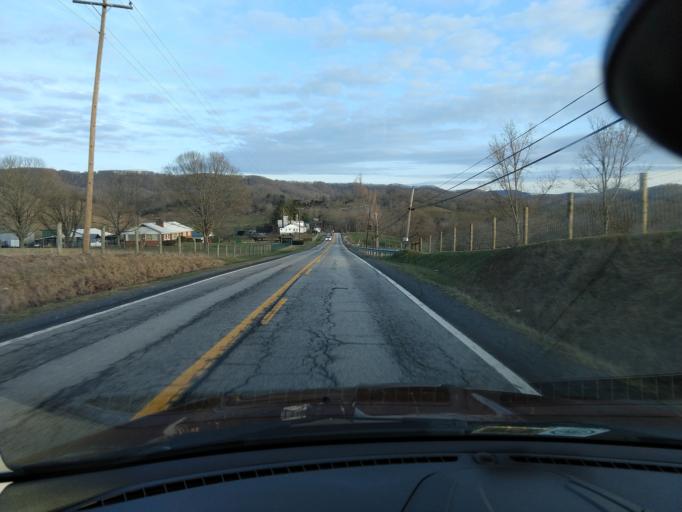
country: US
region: West Virginia
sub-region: Greenbrier County
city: Lewisburg
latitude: 37.9696
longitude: -80.3832
